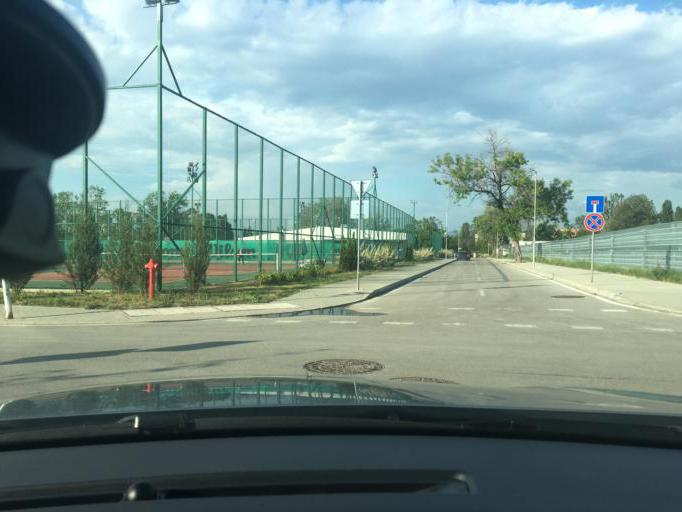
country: BG
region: Sofia-Capital
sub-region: Stolichna Obshtina
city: Sofia
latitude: 42.6686
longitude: 23.3744
